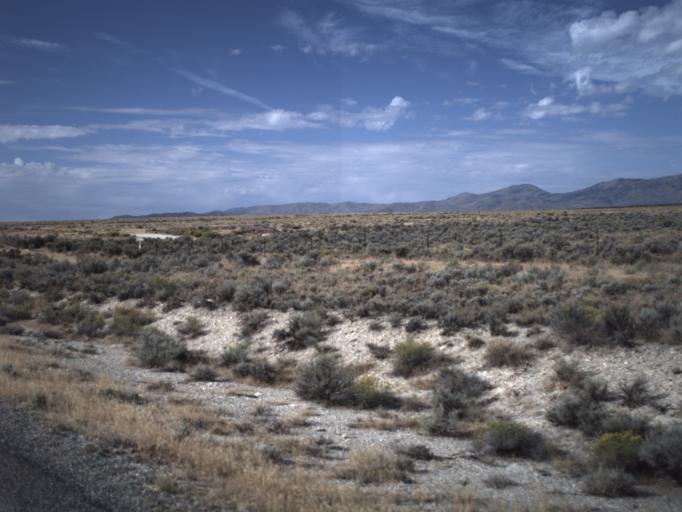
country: US
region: Idaho
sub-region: Cassia County
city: Burley
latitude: 41.7357
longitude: -113.5212
